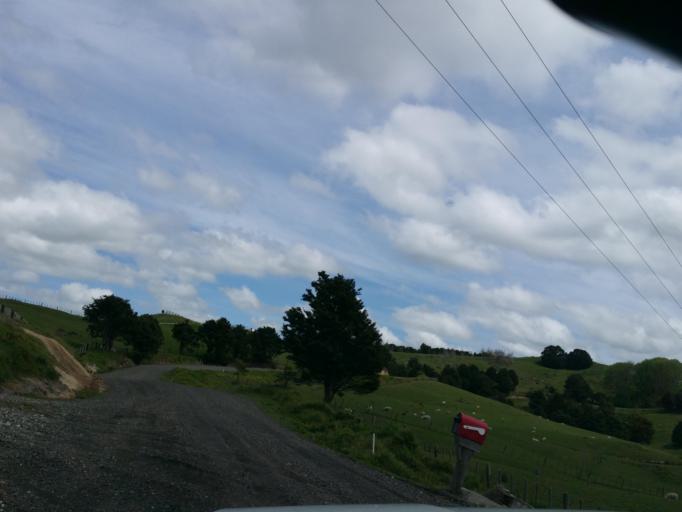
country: NZ
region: Northland
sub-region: Kaipara District
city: Dargaville
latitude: -35.9219
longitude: 174.0721
